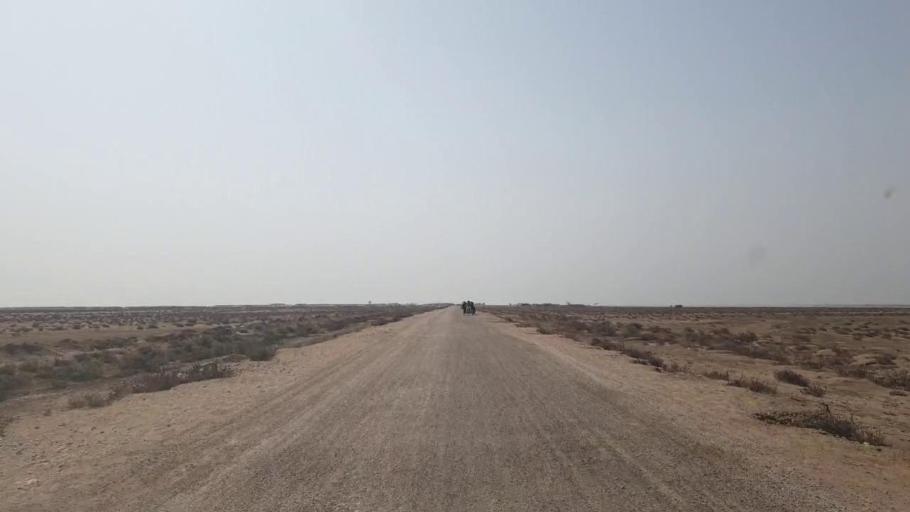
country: PK
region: Sindh
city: Jati
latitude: 24.3499
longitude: 68.5936
